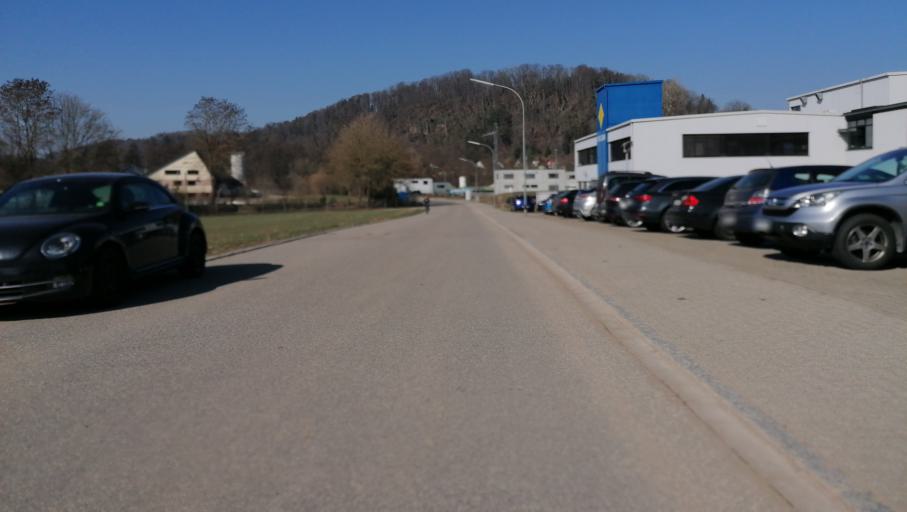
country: DE
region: Baden-Wuerttemberg
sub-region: Freiburg Region
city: Schworstadt
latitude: 47.5807
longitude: 7.9080
